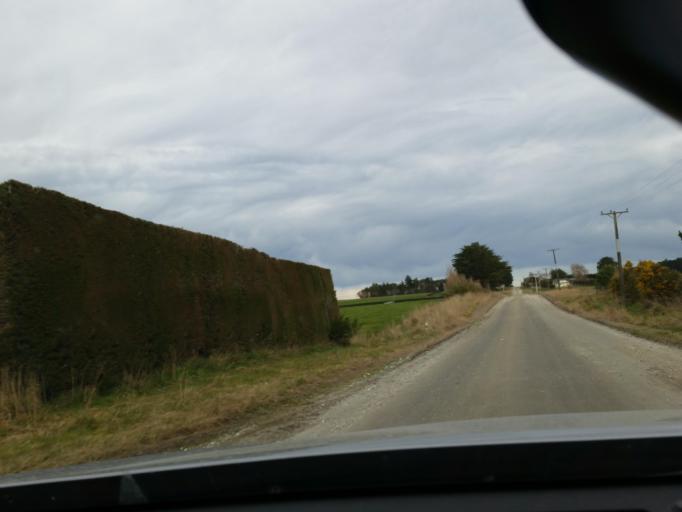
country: NZ
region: Southland
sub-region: Invercargill City
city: Invercargill
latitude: -46.4114
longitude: 168.5060
